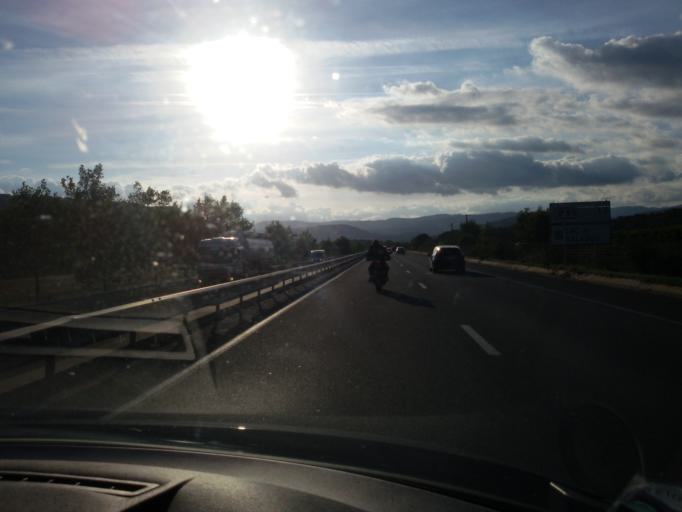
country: FR
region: Languedoc-Roussillon
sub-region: Departement de l'Herault
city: Nebian
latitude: 43.6790
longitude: 3.4010
